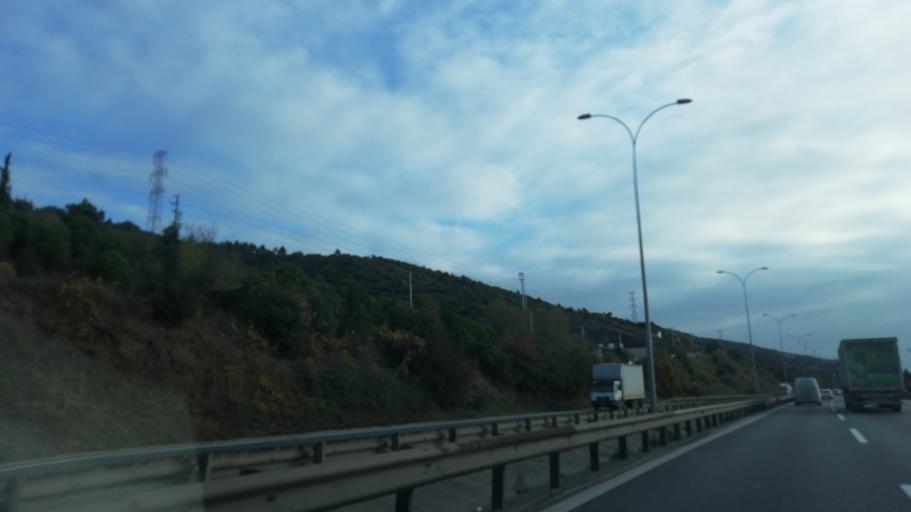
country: TR
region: Kocaeli
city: Ulasli
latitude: 40.7799
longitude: 29.6894
